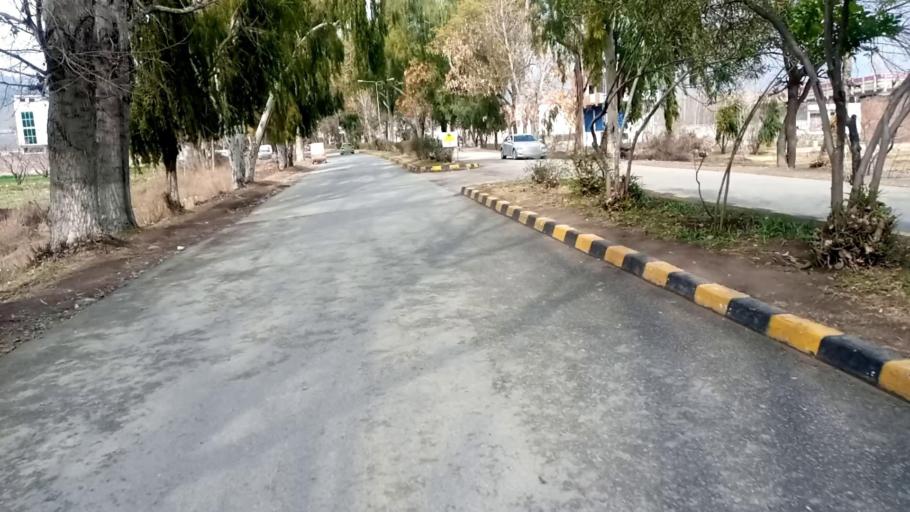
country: PK
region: Khyber Pakhtunkhwa
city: Mingora
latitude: 34.8155
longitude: 72.3414
